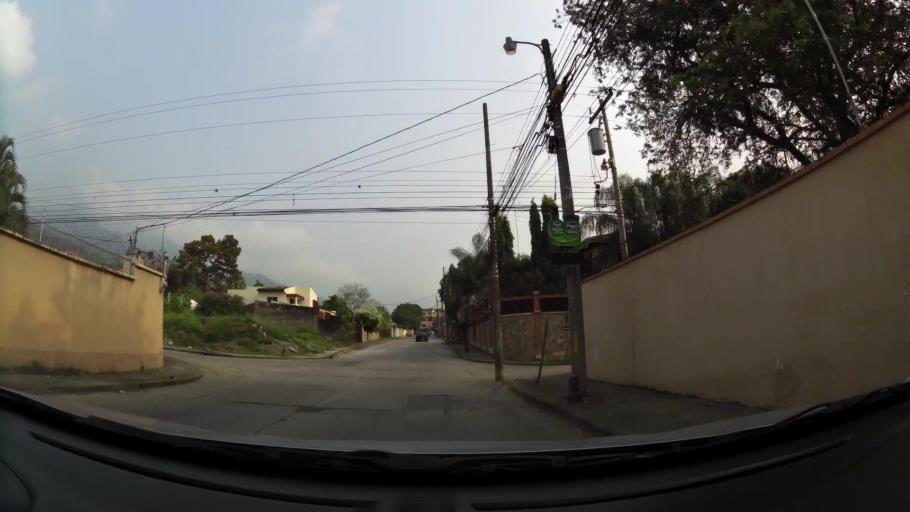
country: HN
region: Cortes
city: Armenta
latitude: 15.4960
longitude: -88.0456
